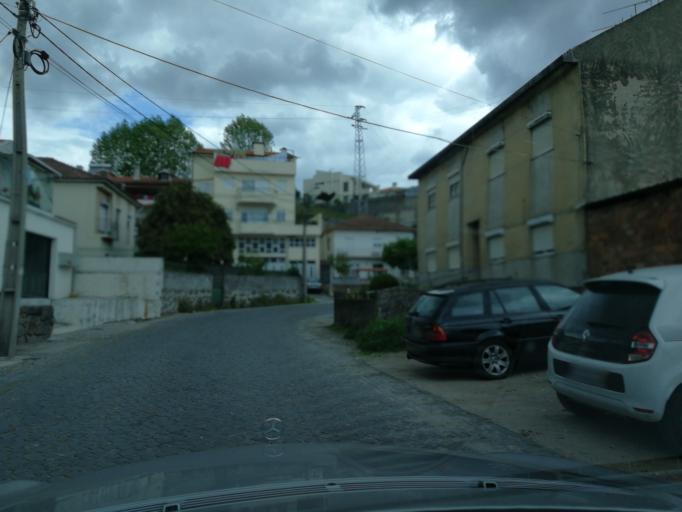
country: PT
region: Braga
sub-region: Braga
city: Braga
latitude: 41.5351
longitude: -8.4203
